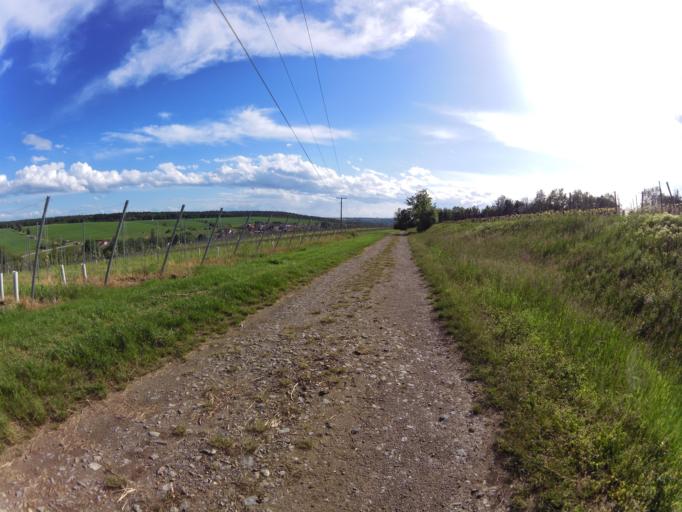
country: DE
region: Bavaria
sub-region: Regierungsbezirk Unterfranken
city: Volkach
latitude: 49.8778
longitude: 10.2652
